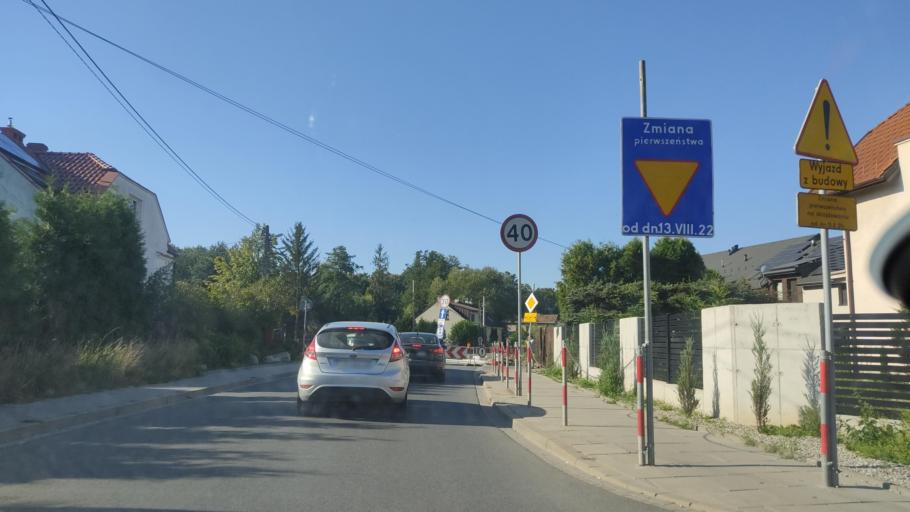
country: PL
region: Lesser Poland Voivodeship
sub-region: Powiat krakowski
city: Zielonki
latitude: 50.0965
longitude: 19.9409
